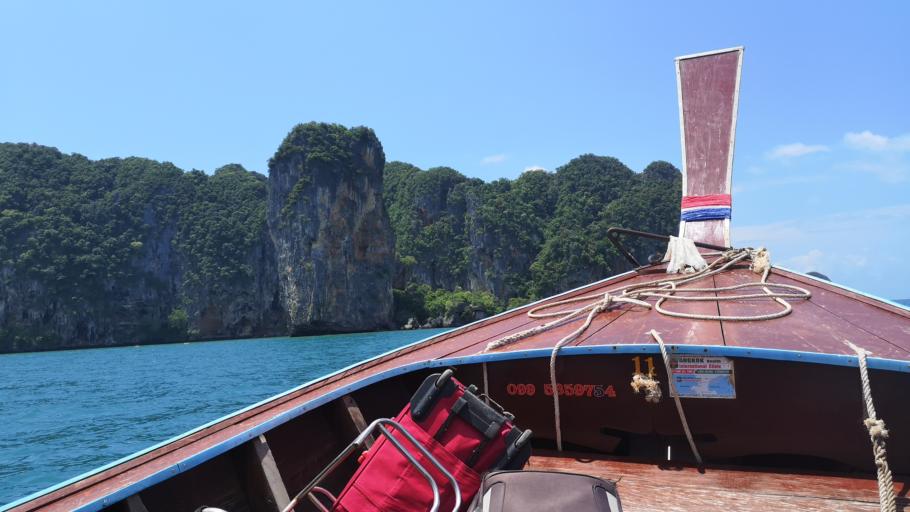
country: TH
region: Phangnga
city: Ban Ao Nang
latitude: 8.0201
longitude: 98.8231
